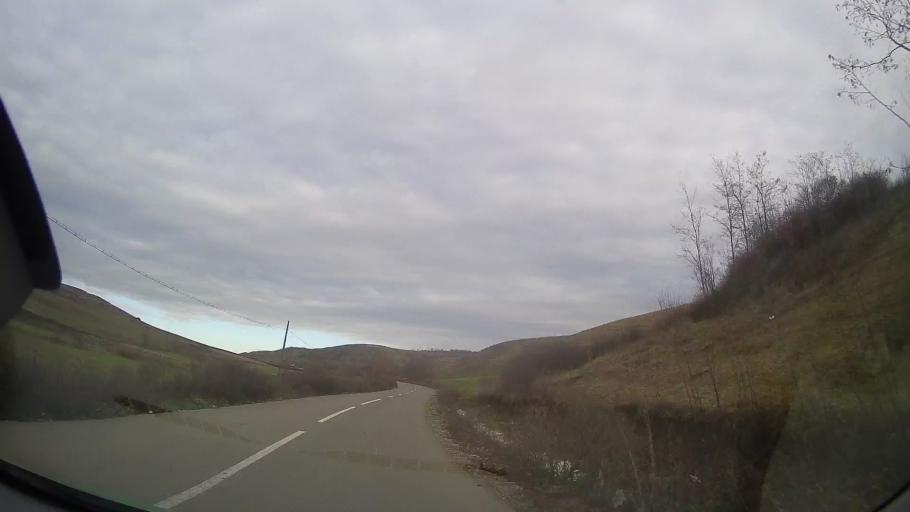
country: RO
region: Bistrita-Nasaud
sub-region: Comuna Silvasu de Campie
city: Silvasu de Campie
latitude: 46.8240
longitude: 24.3035
